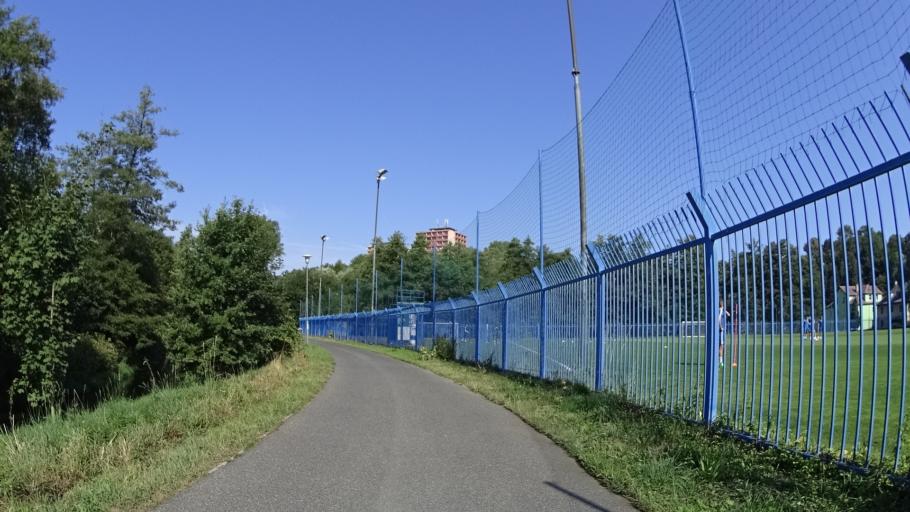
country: CZ
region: Liberecky
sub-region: Okres Liberec
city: Liberec
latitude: 50.7784
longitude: 15.0508
